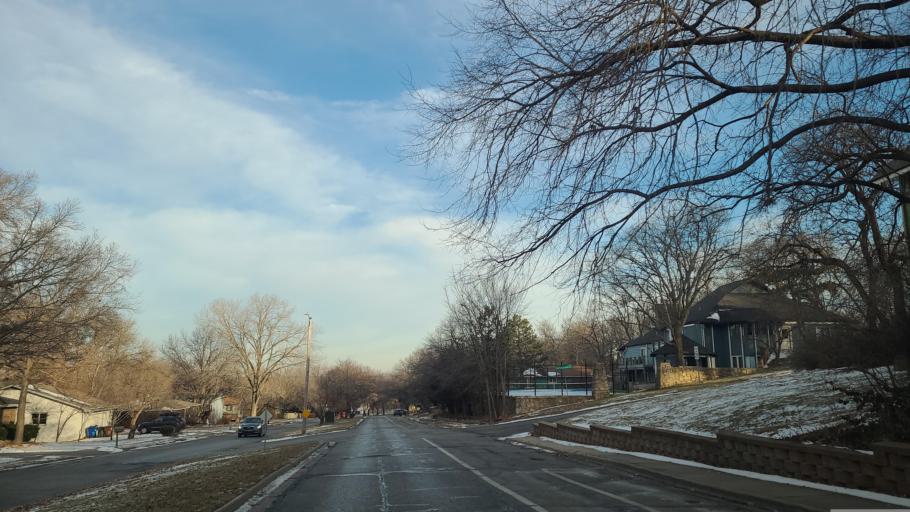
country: US
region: Kansas
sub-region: Douglas County
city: Lawrence
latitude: 38.9779
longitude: -95.2714
